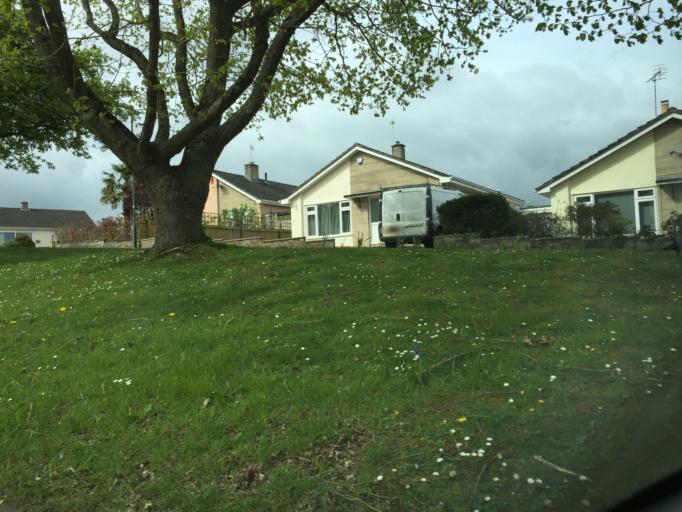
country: GB
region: England
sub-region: Bath and North East Somerset
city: Midsomer Norton
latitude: 51.2878
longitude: -2.4920
